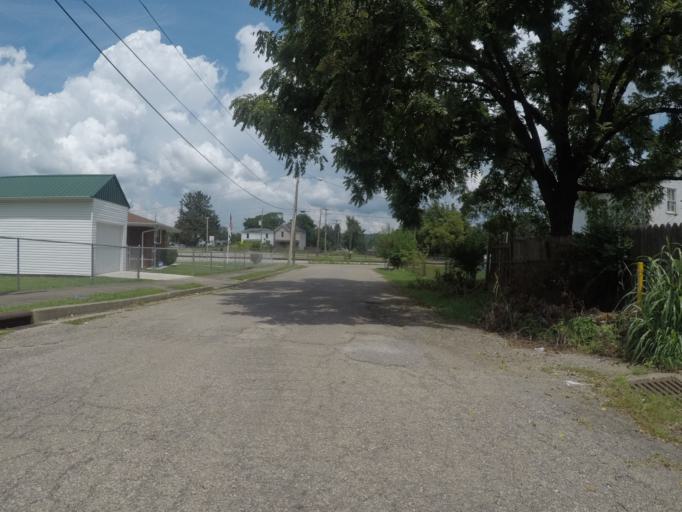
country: US
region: West Virginia
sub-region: Cabell County
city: Huntington
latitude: 38.4262
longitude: -82.3829
